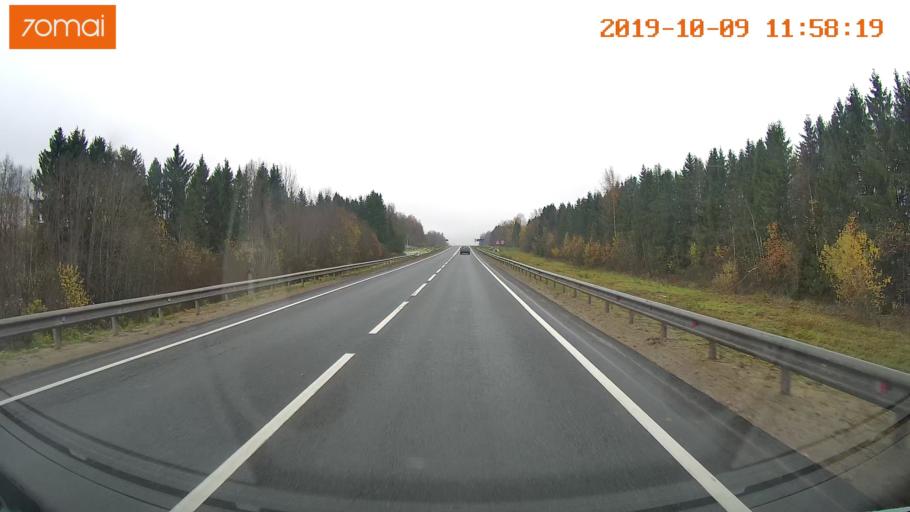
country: RU
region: Vologda
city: Gryazovets
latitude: 58.7198
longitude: 40.2963
